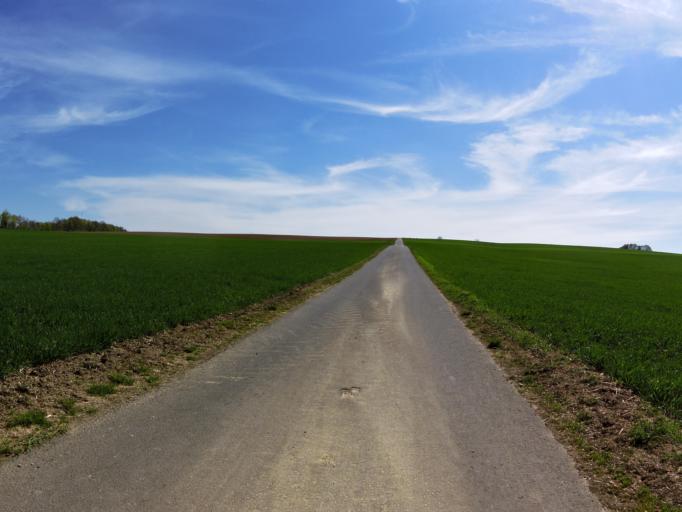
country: DE
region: Bavaria
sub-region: Regierungsbezirk Unterfranken
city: Rottendorf
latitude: 49.7988
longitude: 10.0480
